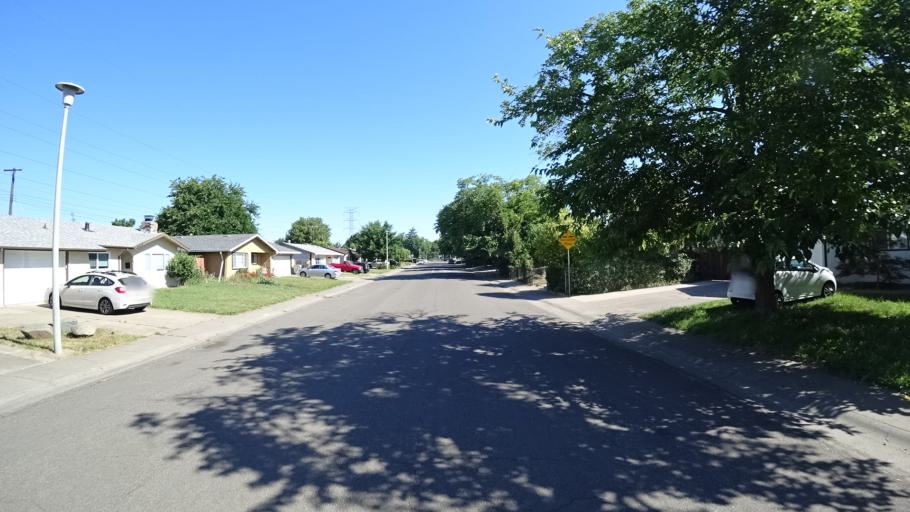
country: US
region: California
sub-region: Sacramento County
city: Rosemont
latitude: 38.5517
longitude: -121.3900
